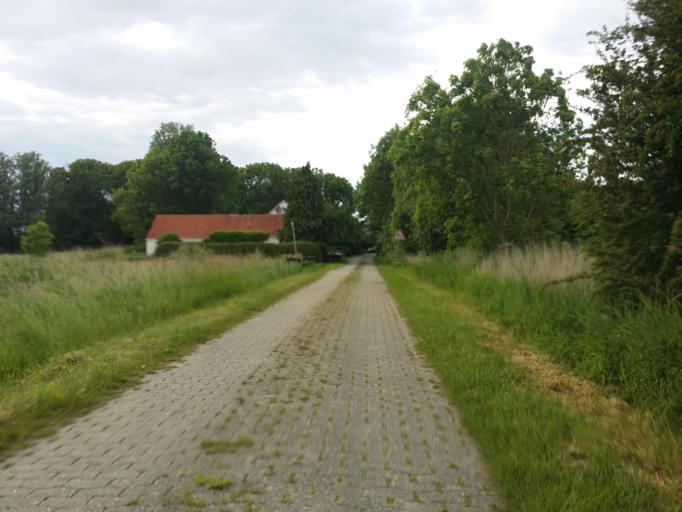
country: DE
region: Lower Saxony
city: Werdum
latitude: 53.6504
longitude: 7.7806
